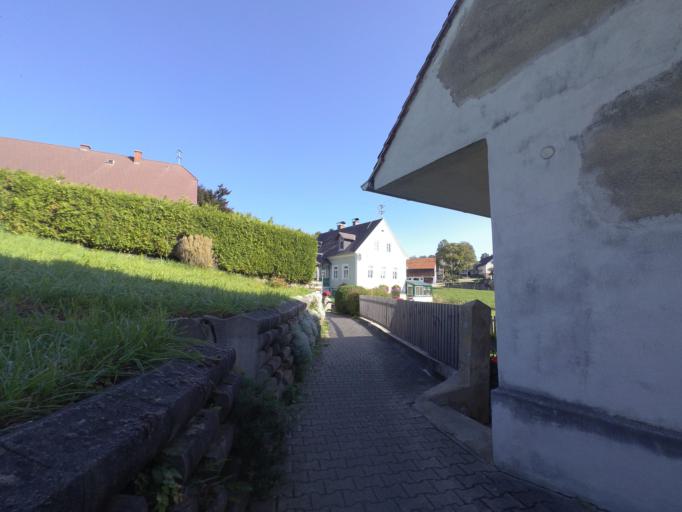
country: AT
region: Styria
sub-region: Politischer Bezirk Weiz
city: Passail
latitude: 47.2862
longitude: 15.4780
